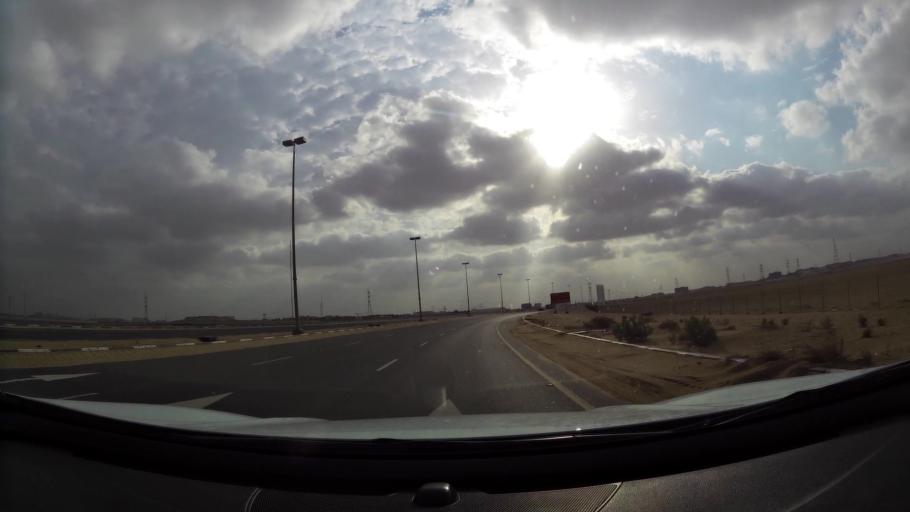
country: AE
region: Abu Dhabi
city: Abu Dhabi
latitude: 24.3468
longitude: 54.6036
